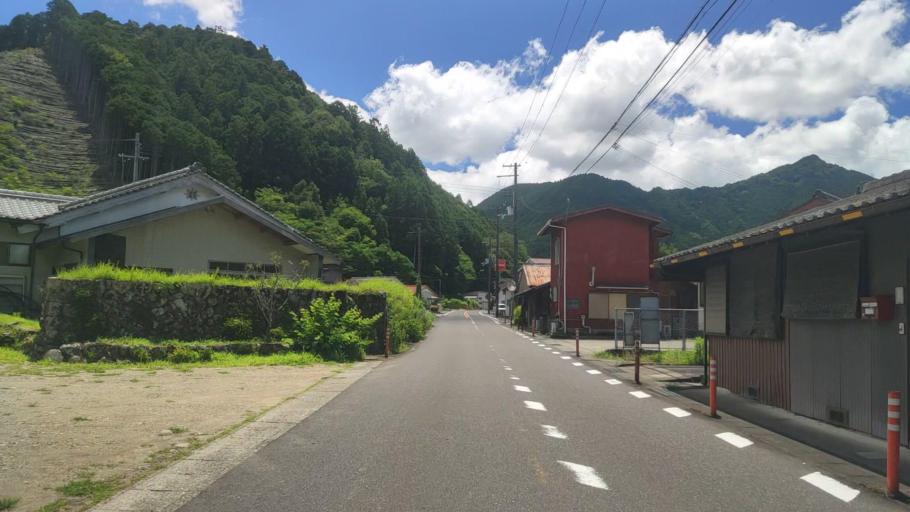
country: JP
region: Mie
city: Owase
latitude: 33.9843
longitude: 136.0486
